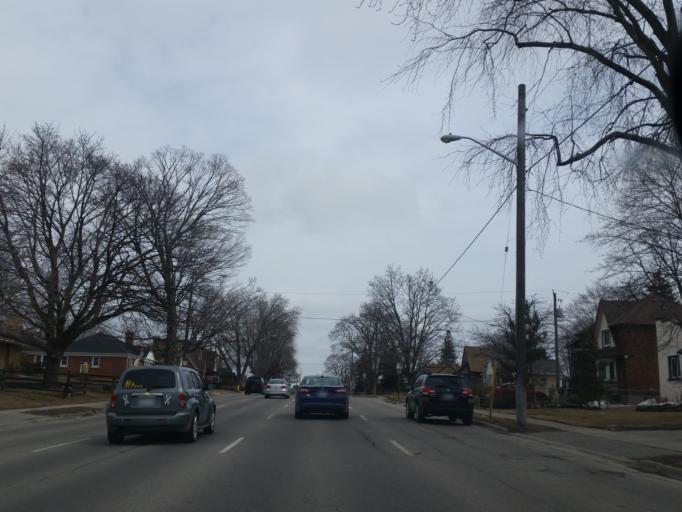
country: CA
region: Ontario
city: Oshawa
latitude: 43.9012
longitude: -78.8480
